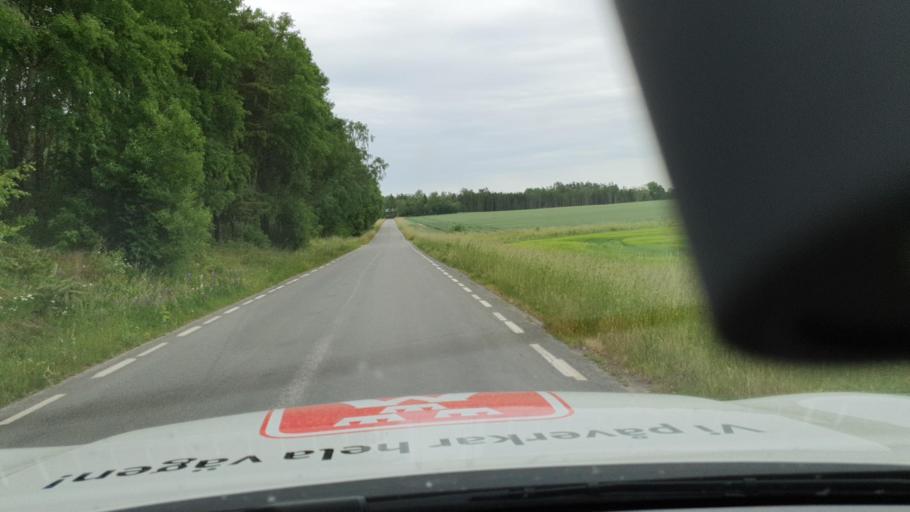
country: SE
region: Vaestra Goetaland
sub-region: Tibro Kommun
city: Tibro
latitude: 58.3423
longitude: 14.1075
